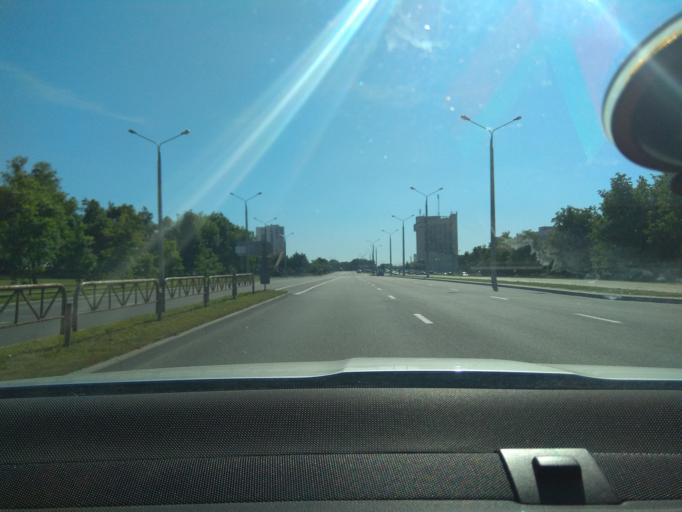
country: BY
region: Grodnenskaya
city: Hrodna
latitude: 53.6522
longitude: 23.7905
